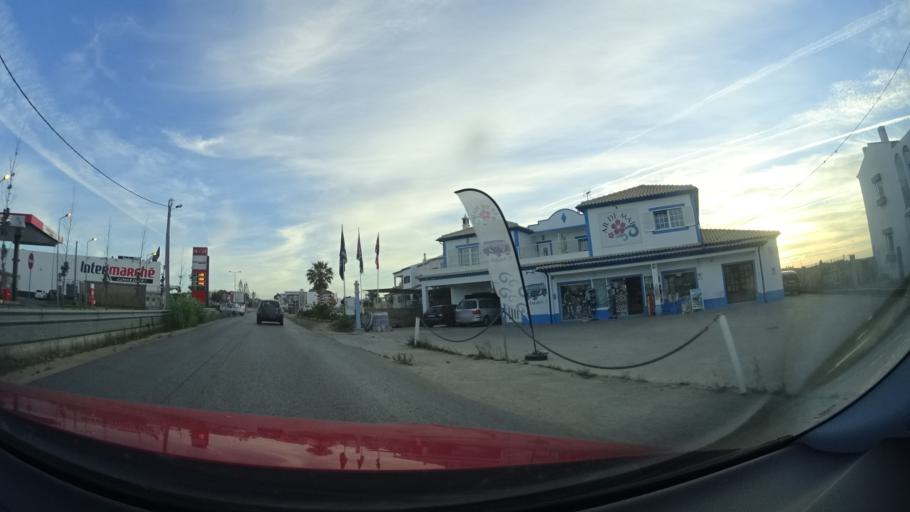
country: PT
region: Faro
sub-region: Vila do Bispo
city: Sagres
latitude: 37.0158
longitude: -8.9415
